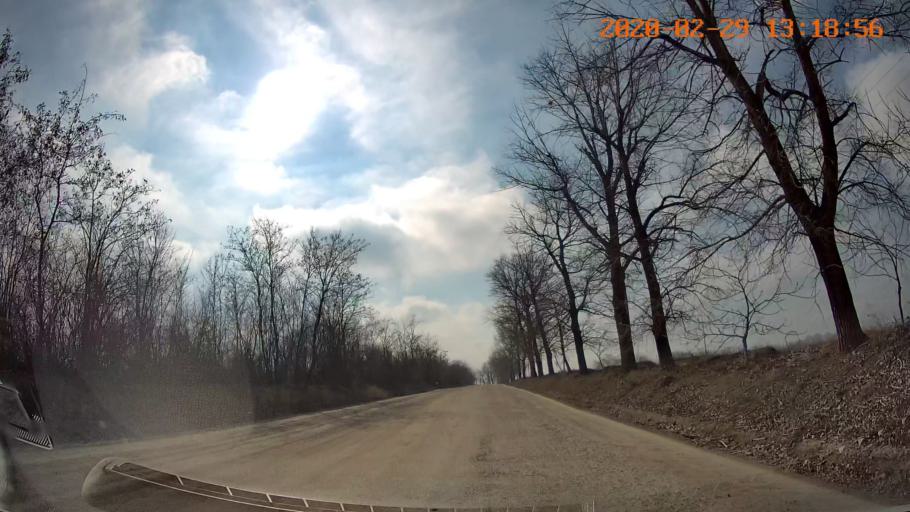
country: MD
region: Telenesti
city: Camenca
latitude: 47.9917
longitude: 28.6545
